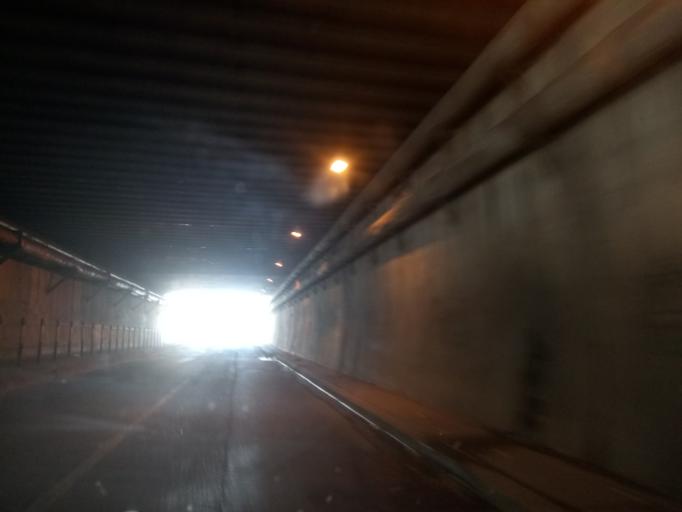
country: RS
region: Central Serbia
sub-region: Belgrade
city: Stari Grad
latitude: 44.8289
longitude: 20.4562
